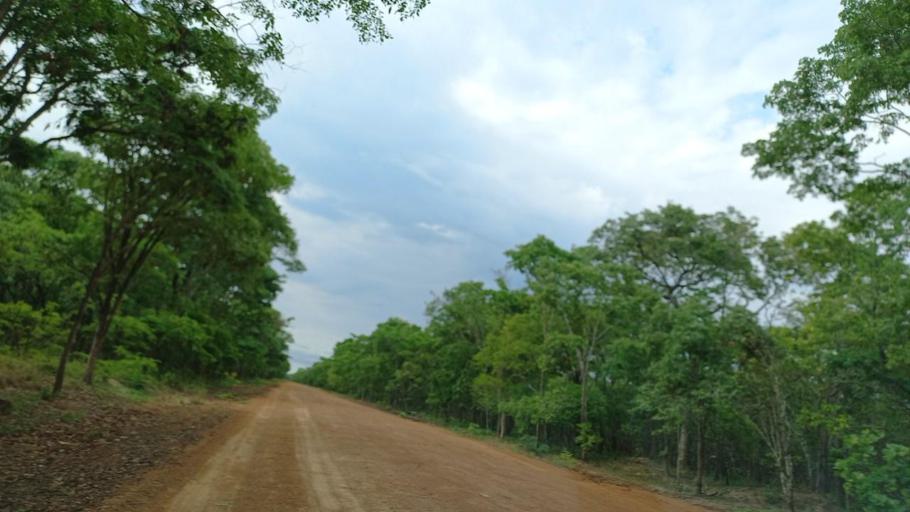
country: ZM
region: North-Western
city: Kalengwa
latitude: -13.3762
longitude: 25.0730
